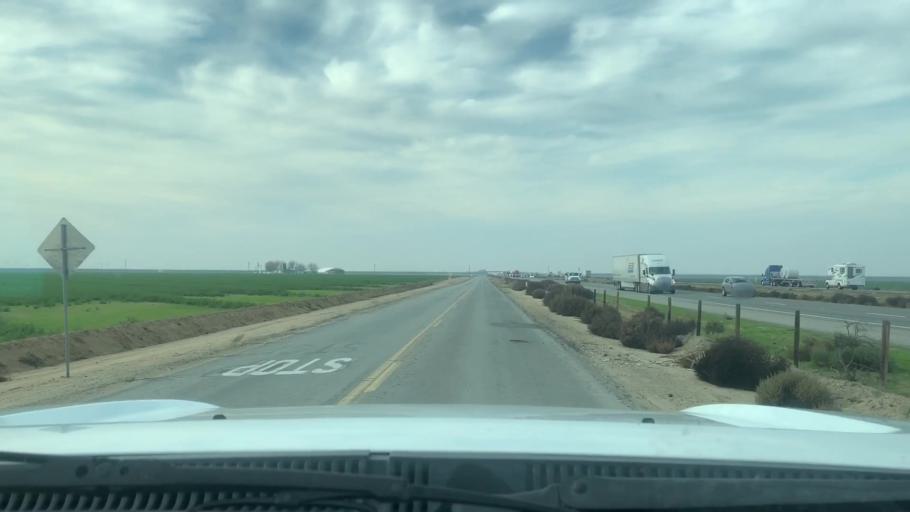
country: US
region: California
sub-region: Kern County
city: Buttonwillow
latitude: 35.4438
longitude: -119.4594
